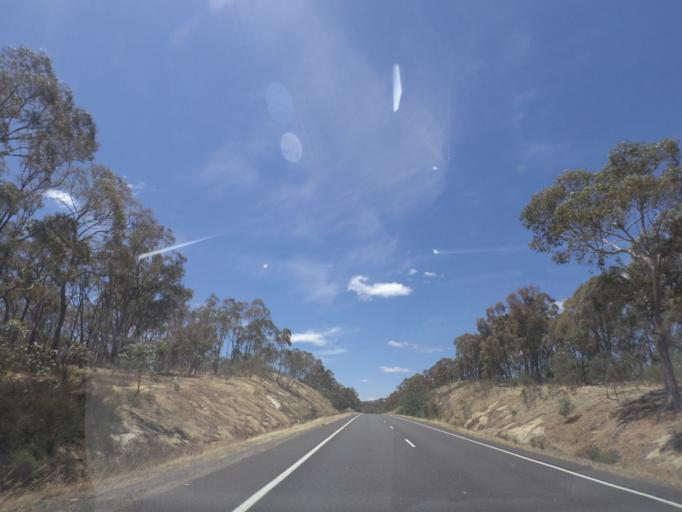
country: AU
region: Victoria
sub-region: Mount Alexander
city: Castlemaine
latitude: -37.1638
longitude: 144.1530
